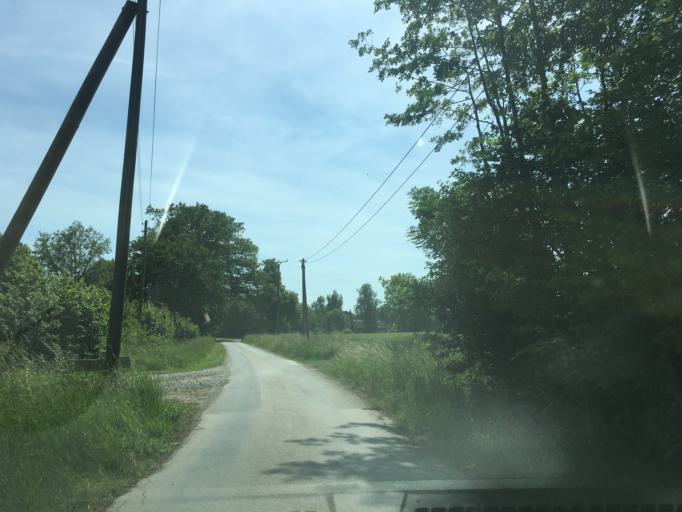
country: DE
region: North Rhine-Westphalia
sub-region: Regierungsbezirk Munster
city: Nordwalde
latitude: 52.0484
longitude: 7.5210
